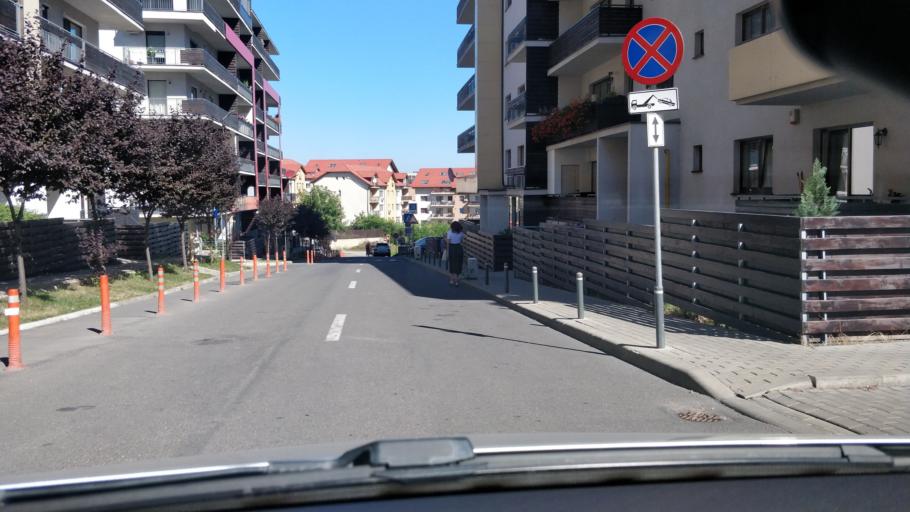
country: RO
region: Cluj
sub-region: Municipiul Cluj-Napoca
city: Cluj-Napoca
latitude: 46.7507
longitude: 23.6000
